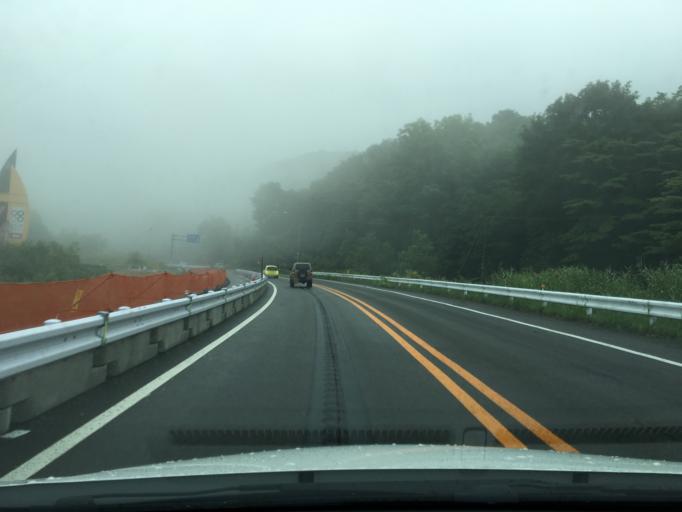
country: JP
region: Yamagata
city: Yonezawa
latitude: 37.8264
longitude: 140.2678
